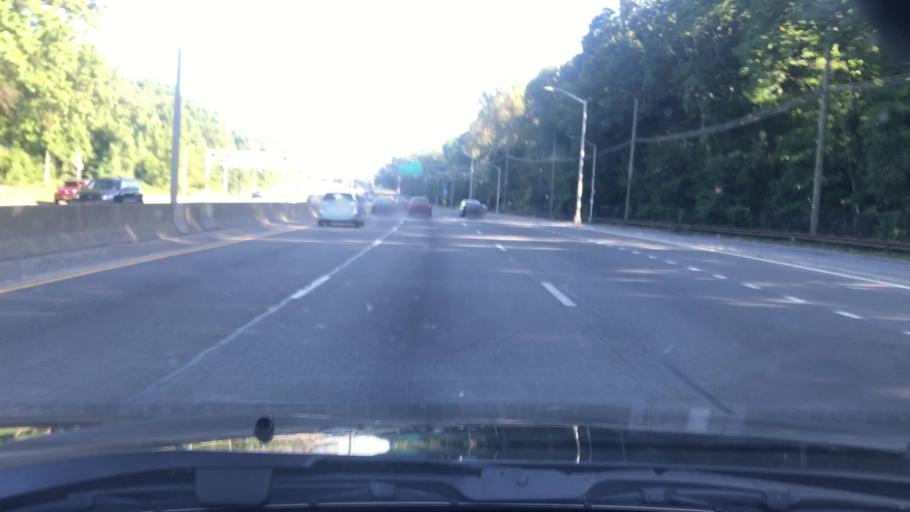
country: US
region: New York
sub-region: Westchester County
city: Yonkers
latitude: 40.8987
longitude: -73.8793
